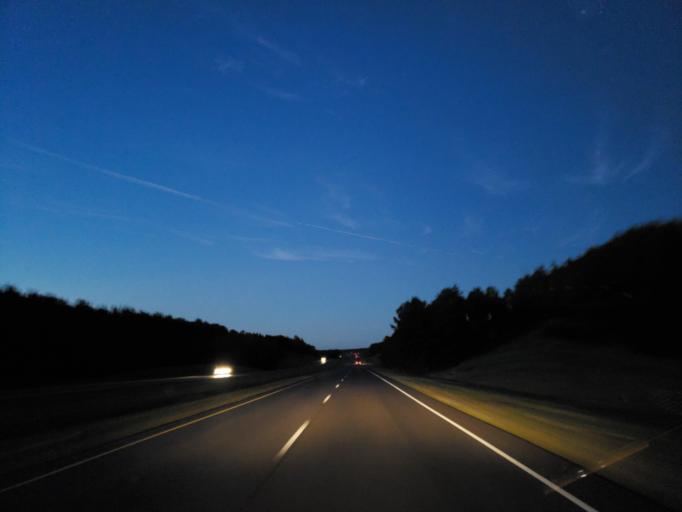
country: US
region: Mississippi
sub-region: Clarke County
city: Quitman
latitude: 32.0231
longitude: -88.6842
